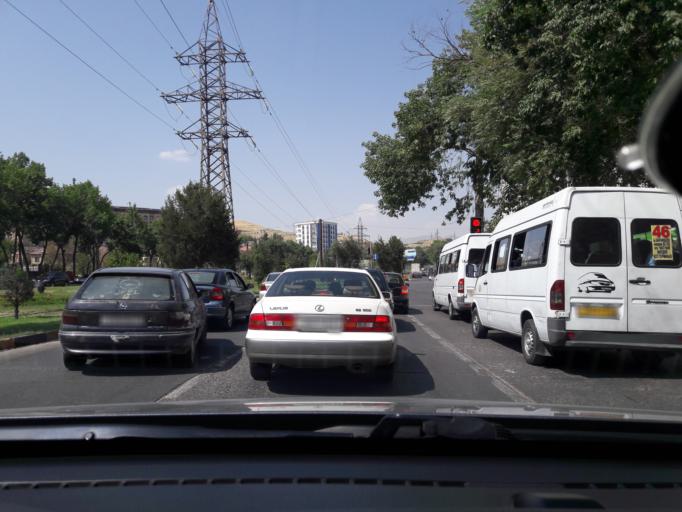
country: TJ
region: Dushanbe
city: Dushanbe
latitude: 38.5893
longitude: 68.7416
